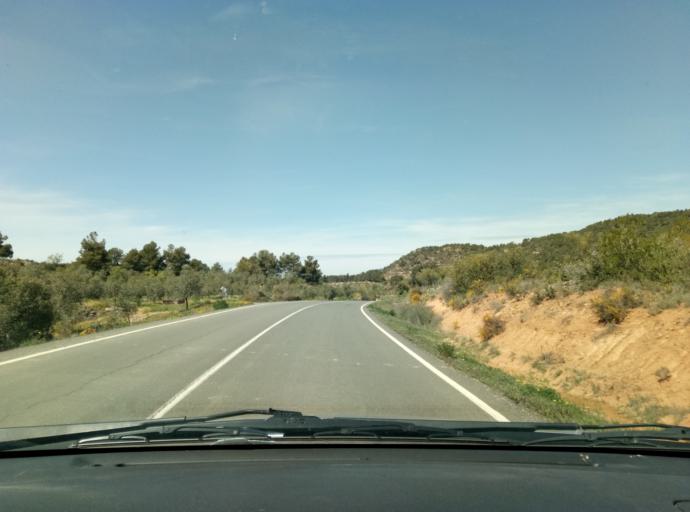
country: ES
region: Catalonia
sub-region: Provincia de Lleida
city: Vinaixa
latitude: 41.4254
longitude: 0.9055
